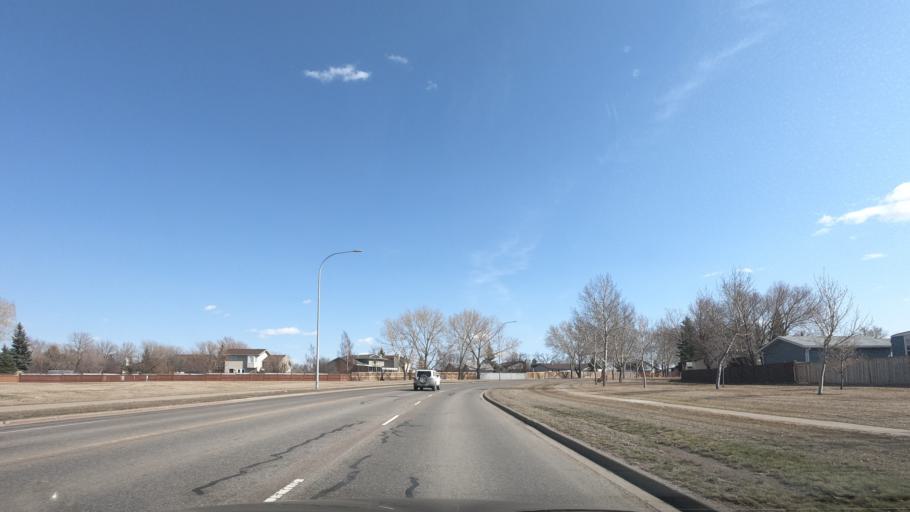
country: CA
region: Alberta
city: Airdrie
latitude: 51.2828
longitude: -113.9903
